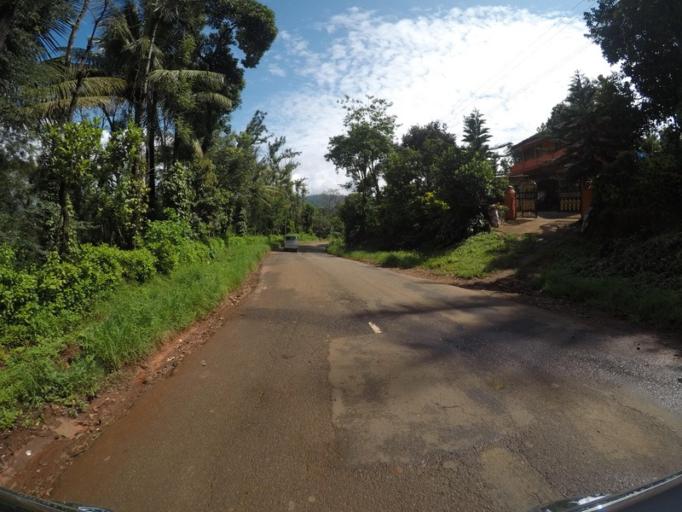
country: IN
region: Karnataka
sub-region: Kodagu
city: Suntikoppa
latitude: 12.5102
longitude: 75.8042
